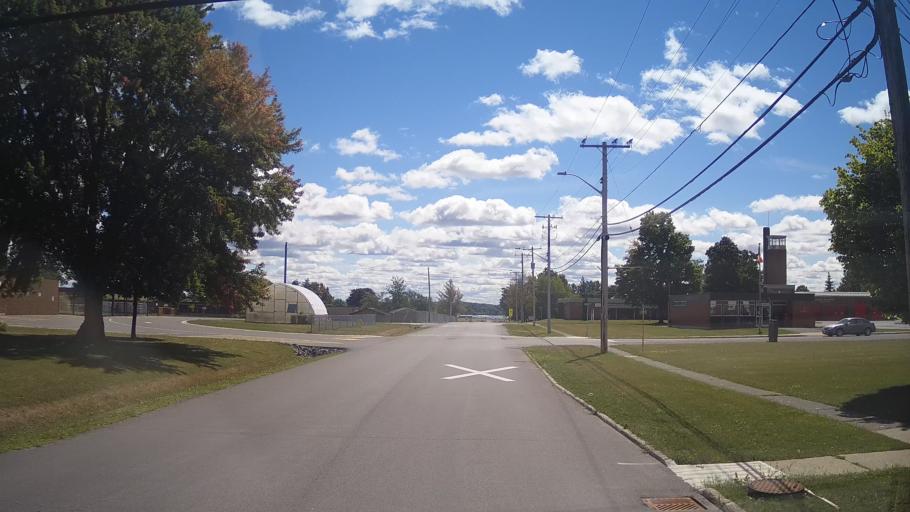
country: US
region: New York
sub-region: St. Lawrence County
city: Ogdensburg
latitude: 44.8505
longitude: -75.3156
